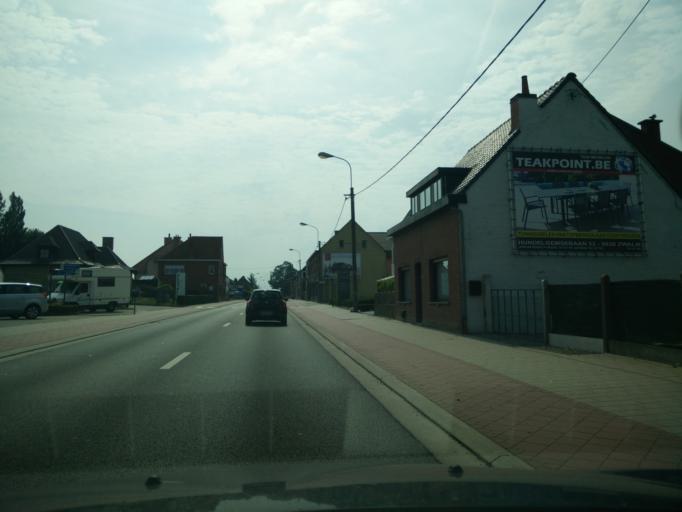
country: BE
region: Flanders
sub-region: Provincie Oost-Vlaanderen
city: Merelbeke
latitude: 50.9878
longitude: 3.7464
